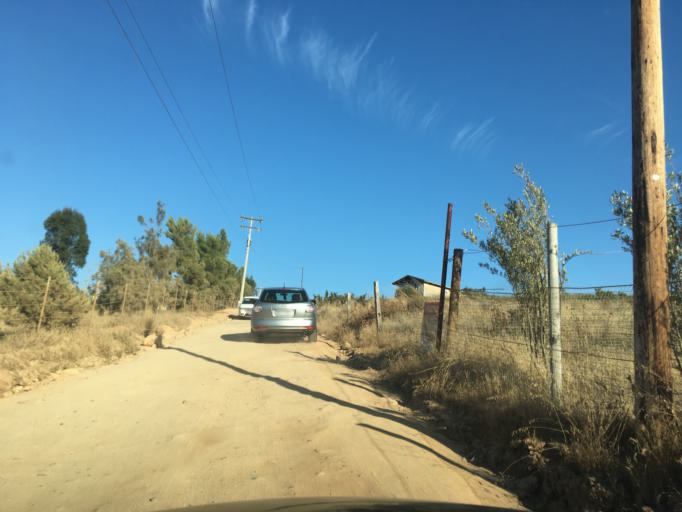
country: MX
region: Baja California
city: El Sauzal
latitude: 32.0189
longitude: -116.6707
